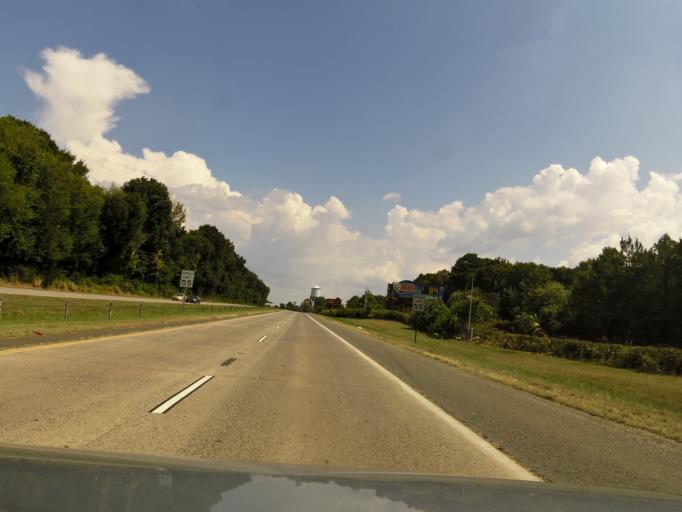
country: US
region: North Carolina
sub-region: Mecklenburg County
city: Charlotte
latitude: 35.2531
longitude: -80.8642
